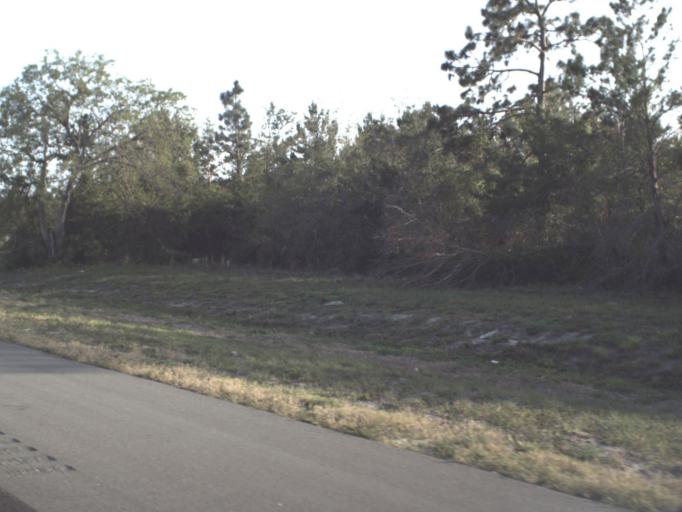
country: US
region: Florida
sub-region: Brevard County
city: Mims
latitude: 28.7425
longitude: -80.8860
